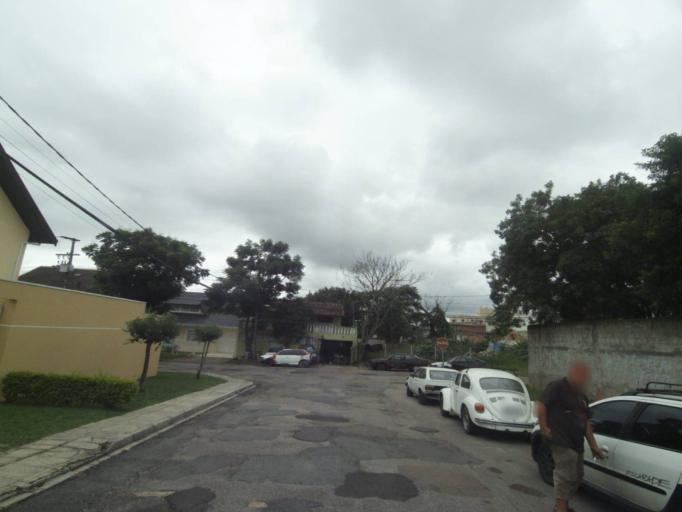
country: BR
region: Parana
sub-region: Curitiba
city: Curitiba
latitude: -25.4917
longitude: -49.3087
